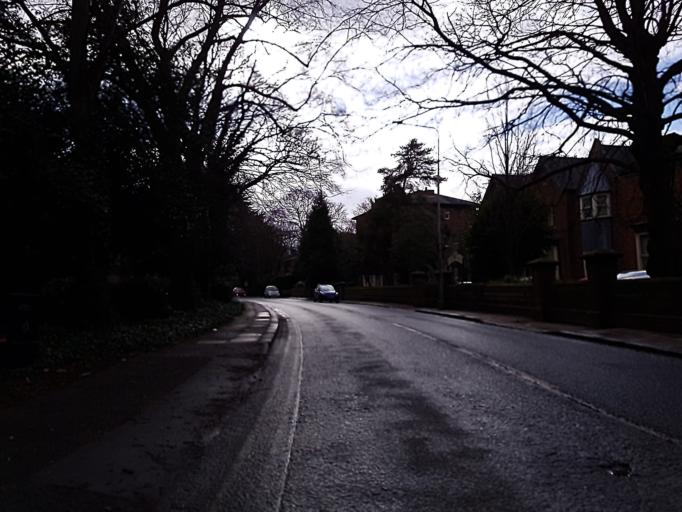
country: GB
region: England
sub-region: North East Lincolnshire
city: Grimbsy
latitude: 53.5611
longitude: -0.0922
